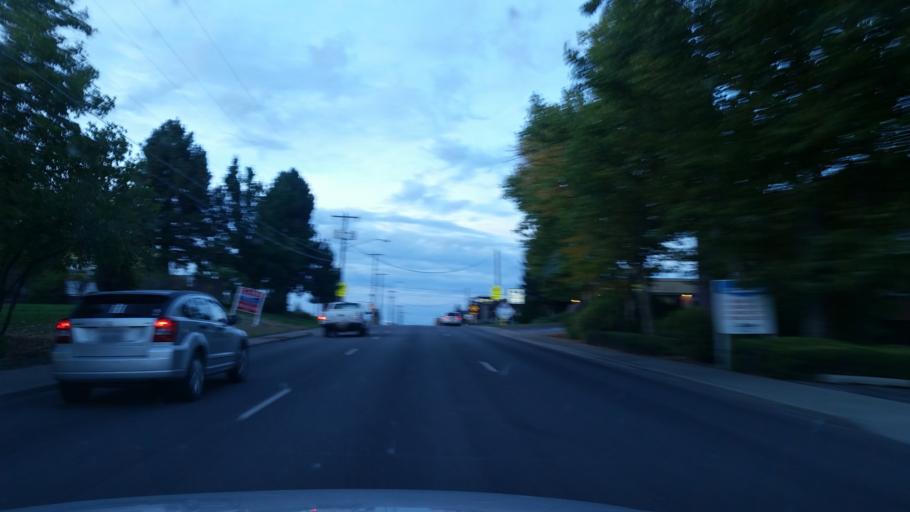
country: US
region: Washington
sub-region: Spokane County
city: Dishman
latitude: 47.6594
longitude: -117.2815
